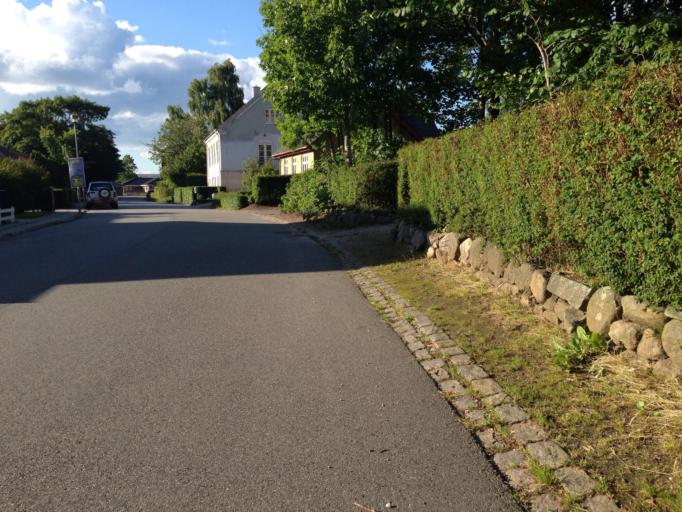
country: DK
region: South Denmark
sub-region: Middelfart Kommune
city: Norre Aby
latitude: 55.4897
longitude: 9.9094
